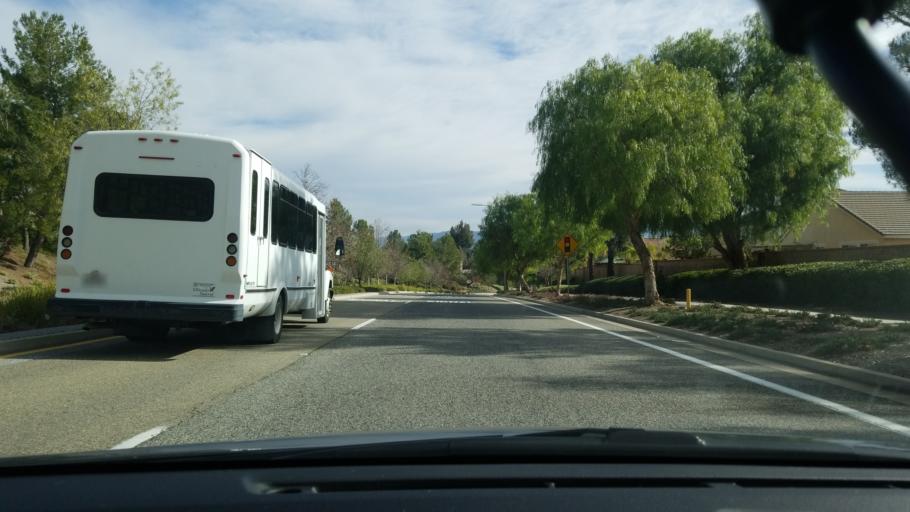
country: US
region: California
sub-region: Riverside County
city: Temecula
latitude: 33.4959
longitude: -117.0848
